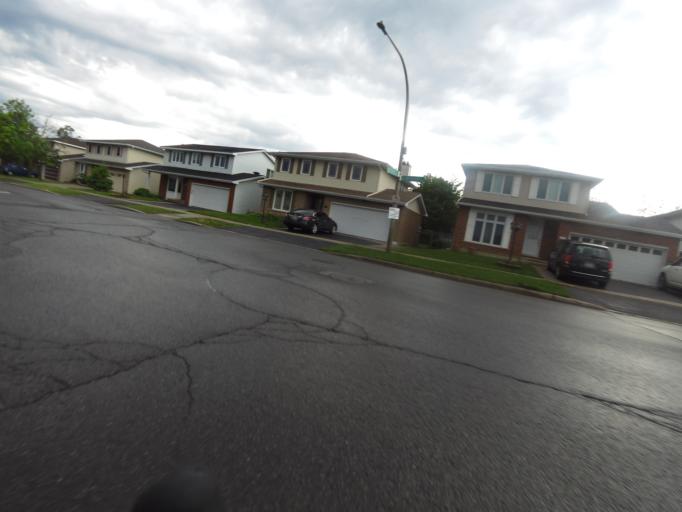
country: CA
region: Ontario
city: Bells Corners
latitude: 45.3354
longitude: -75.7490
